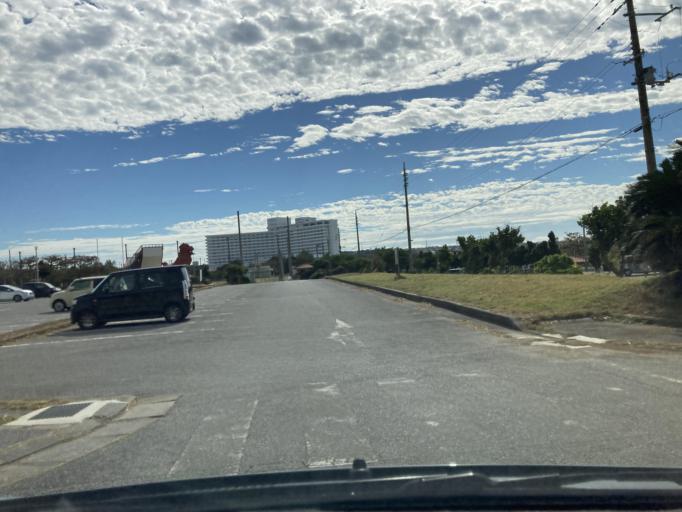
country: JP
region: Okinawa
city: Ishikawa
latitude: 26.4385
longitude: 127.7144
